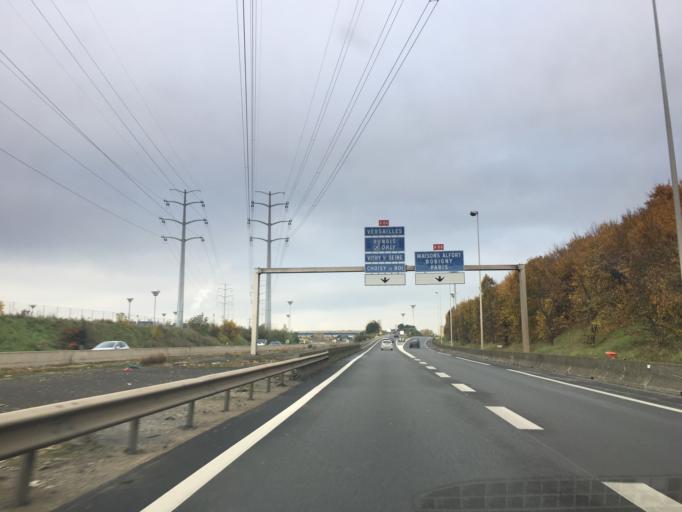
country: FR
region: Ile-de-France
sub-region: Departement du Val-de-Marne
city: Creteil
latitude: 48.7731
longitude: 2.4458
